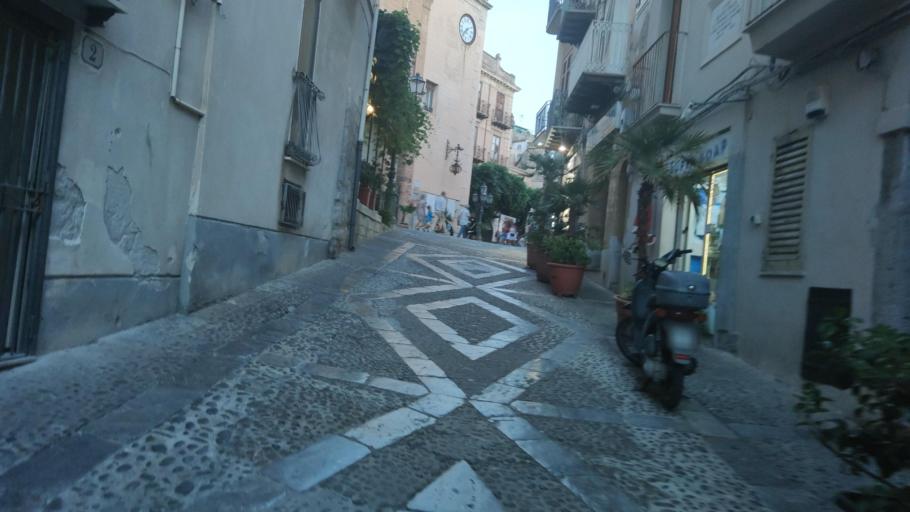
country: IT
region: Sicily
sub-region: Palermo
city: Cefalu
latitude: 38.0372
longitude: 14.0216
